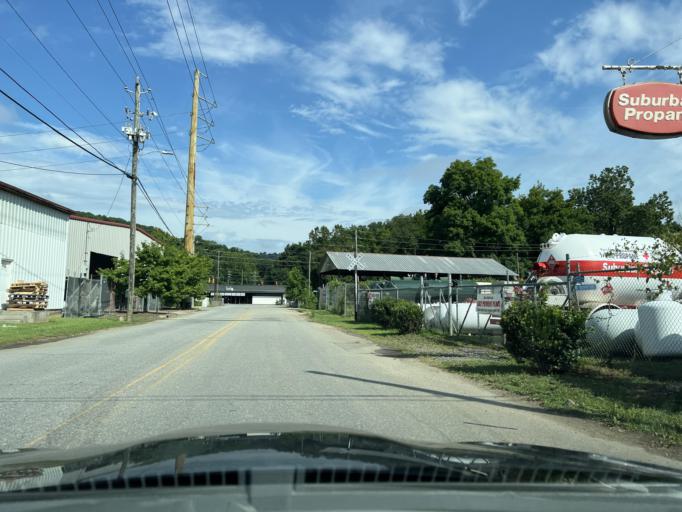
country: US
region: North Carolina
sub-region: Buncombe County
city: Asheville
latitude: 35.5734
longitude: -82.5260
